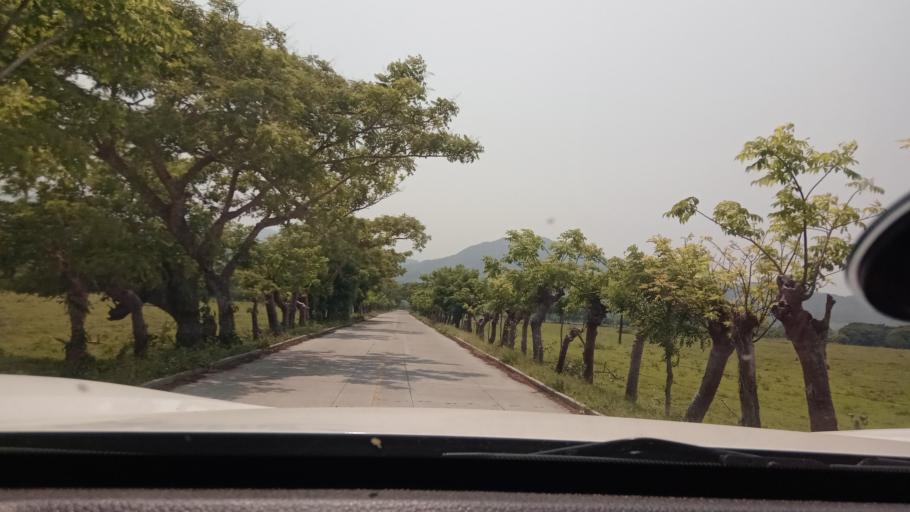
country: MX
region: Veracruz
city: Catemaco
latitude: 18.5627
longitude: -95.0468
